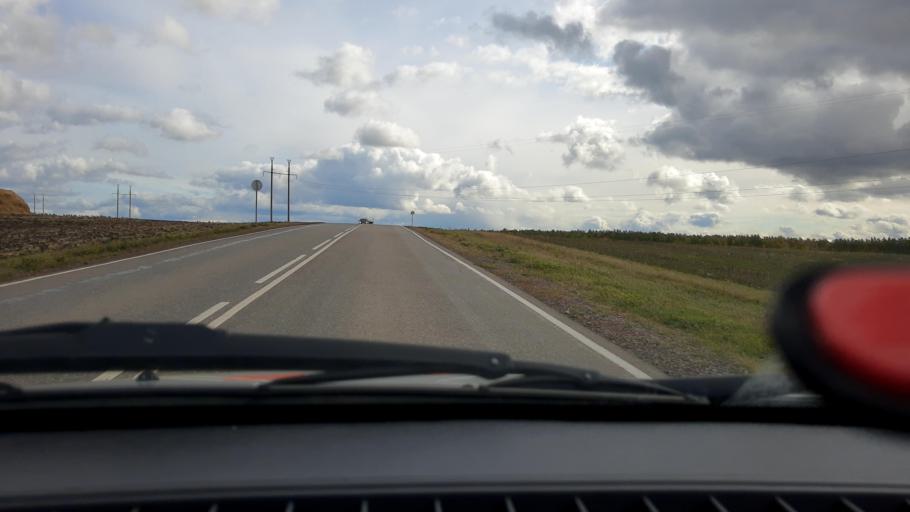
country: RU
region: Bashkortostan
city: Aksakovo
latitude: 53.9418
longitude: 54.4298
